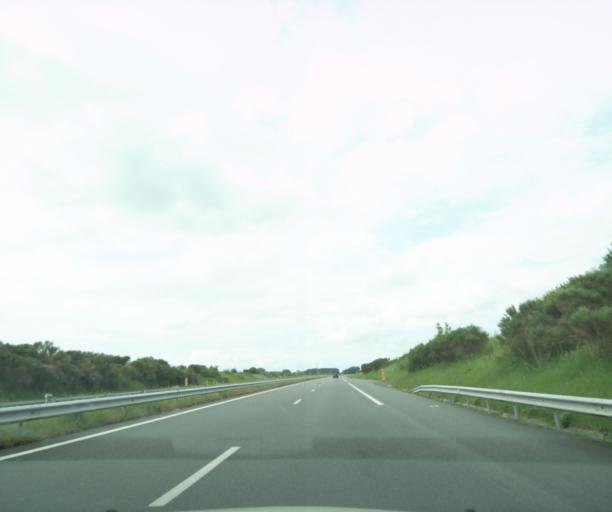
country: FR
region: Centre
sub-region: Departement du Cher
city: Orval
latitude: 46.8024
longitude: 2.4130
